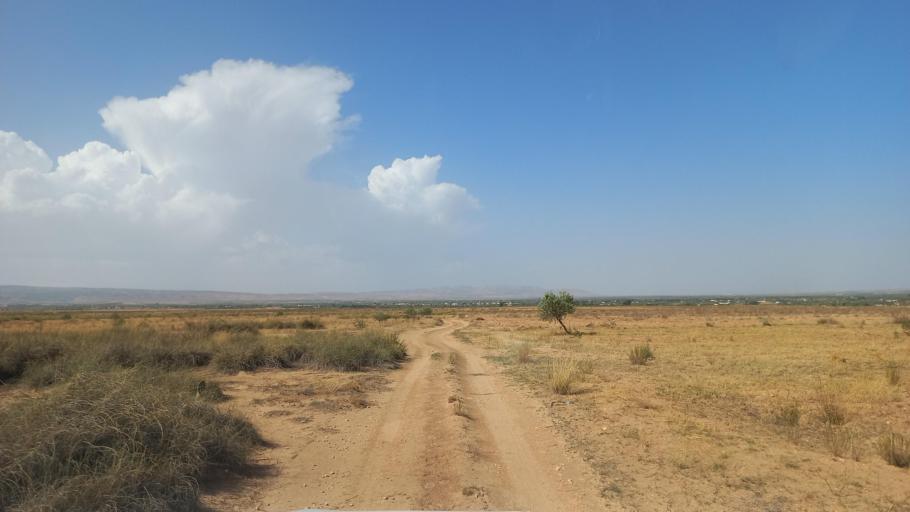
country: TN
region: Al Qasrayn
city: Kasserine
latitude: 35.2150
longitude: 9.0267
